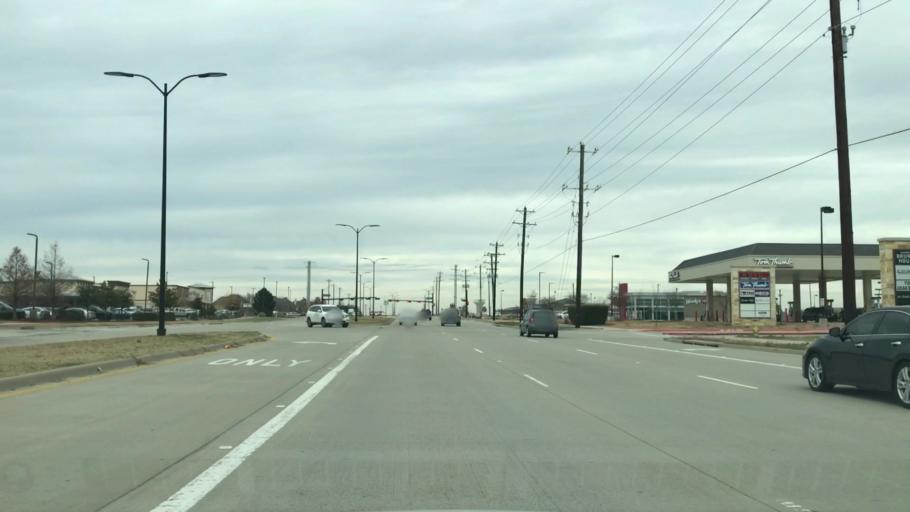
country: US
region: Texas
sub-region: Denton County
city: The Colony
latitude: 33.1244
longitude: -96.8911
